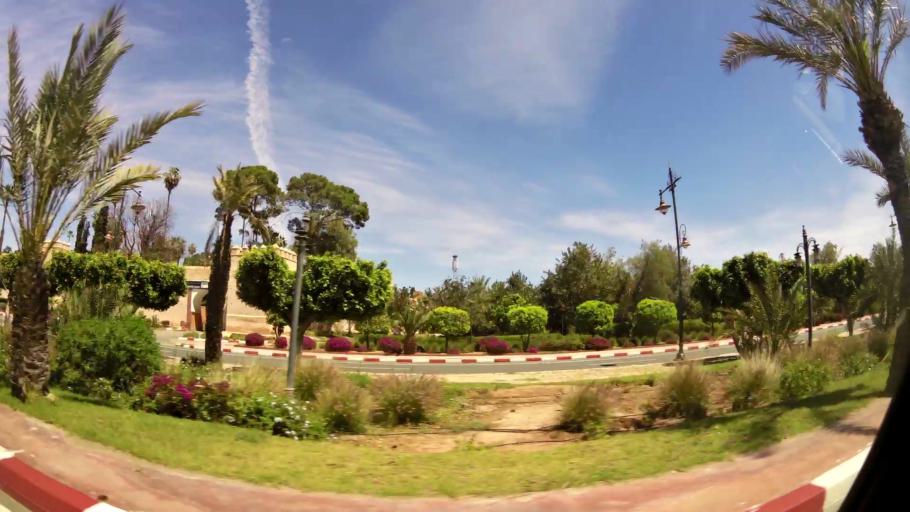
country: MA
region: Marrakech-Tensift-Al Haouz
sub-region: Marrakech
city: Marrakesh
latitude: 31.6170
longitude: -7.9969
